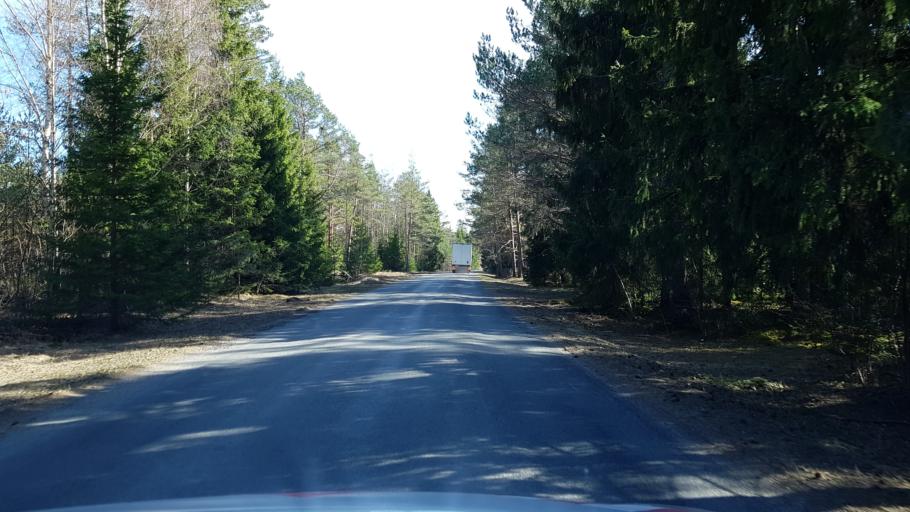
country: EE
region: Harju
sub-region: Nissi vald
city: Riisipere
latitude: 59.0825
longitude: 24.3550
